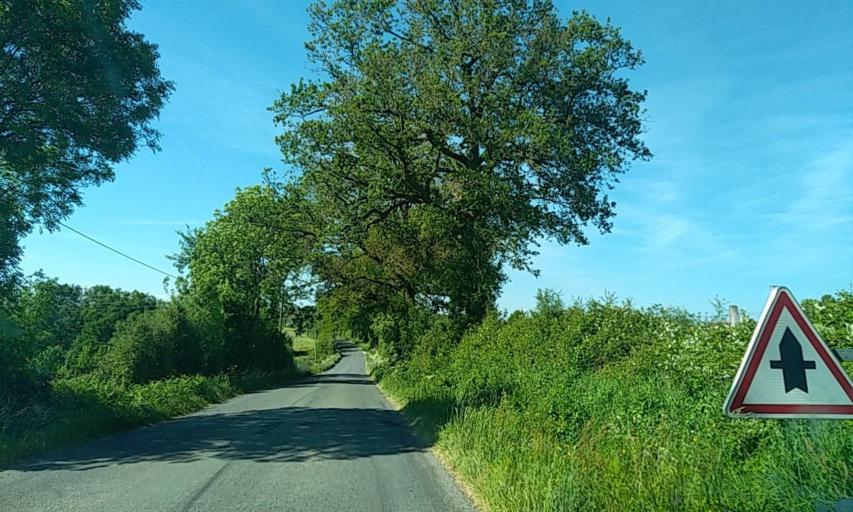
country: FR
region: Poitou-Charentes
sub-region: Departement des Deux-Sevres
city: Boisme
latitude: 46.7929
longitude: -0.4519
